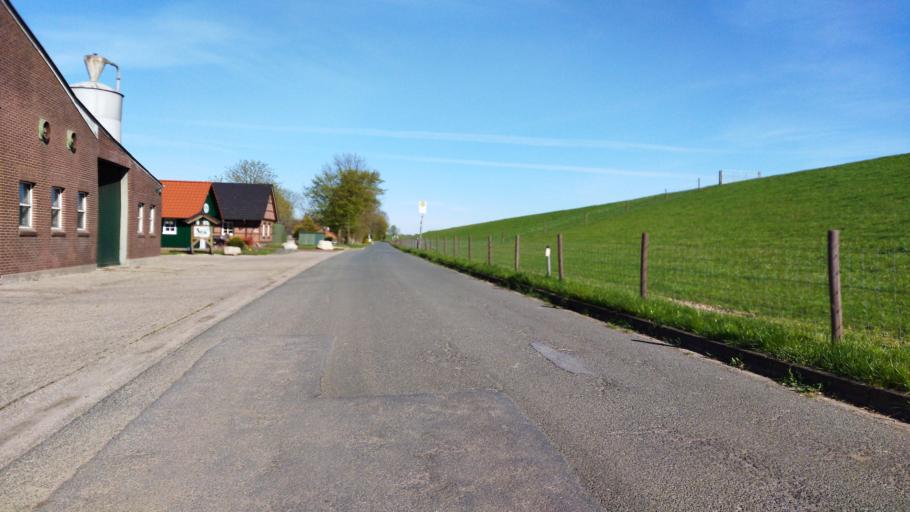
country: DE
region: Lower Saxony
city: Elsfleth
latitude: 53.2179
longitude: 8.4754
